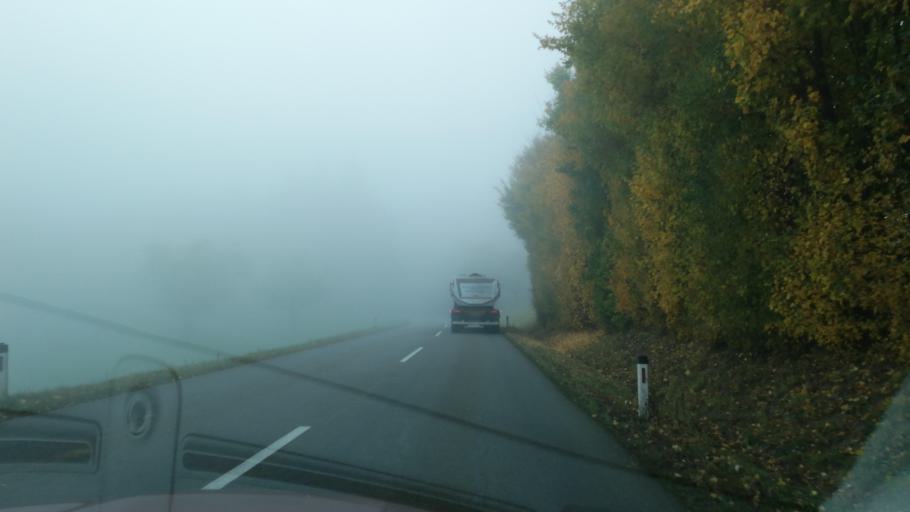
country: AT
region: Upper Austria
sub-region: Politischer Bezirk Grieskirchen
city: Bad Schallerbach
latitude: 48.1790
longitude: 13.9093
